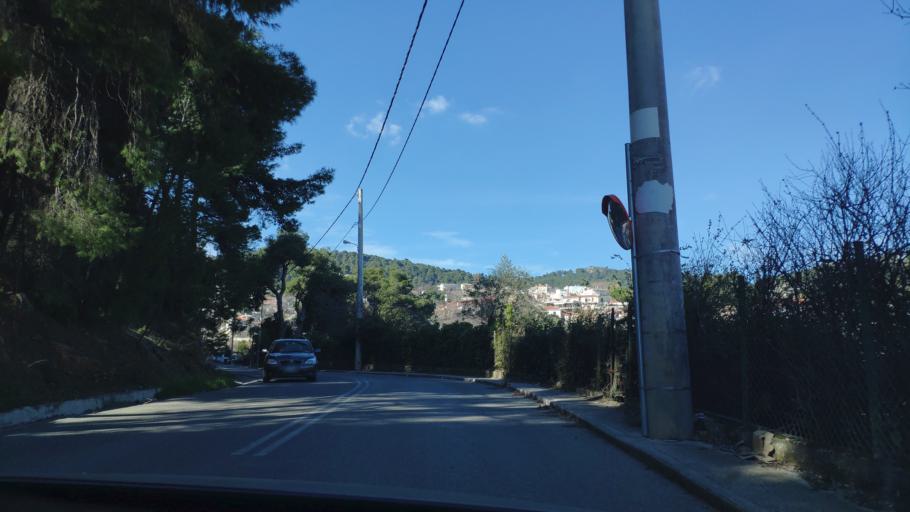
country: GR
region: Attica
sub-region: Nomarchia Anatolikis Attikis
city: Afidnes
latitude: 38.2018
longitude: 23.8394
